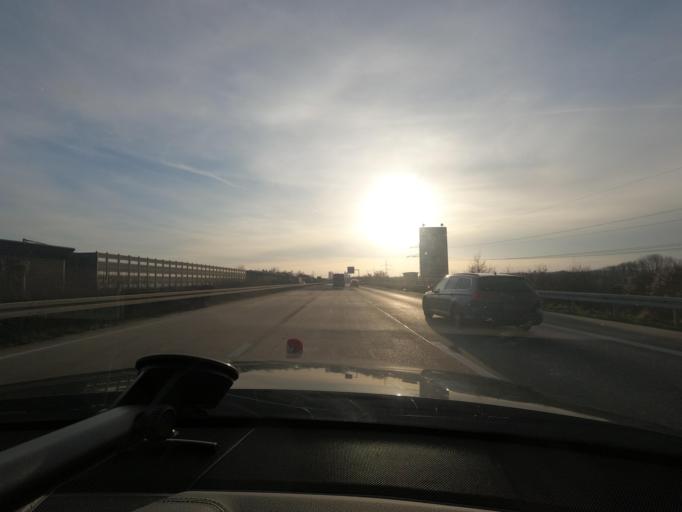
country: DE
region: Lower Saxony
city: Lehrte
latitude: 52.3746
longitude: 9.8961
